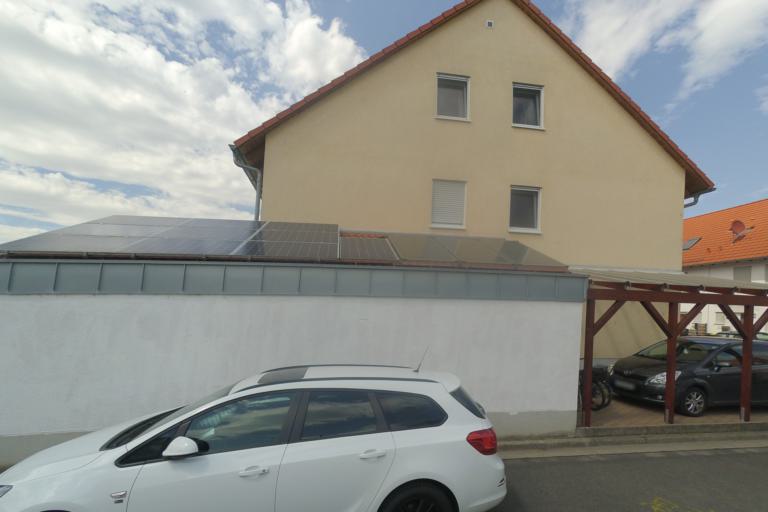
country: DE
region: Rheinland-Pfalz
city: Frankenthal
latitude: 49.5154
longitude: 8.3380
